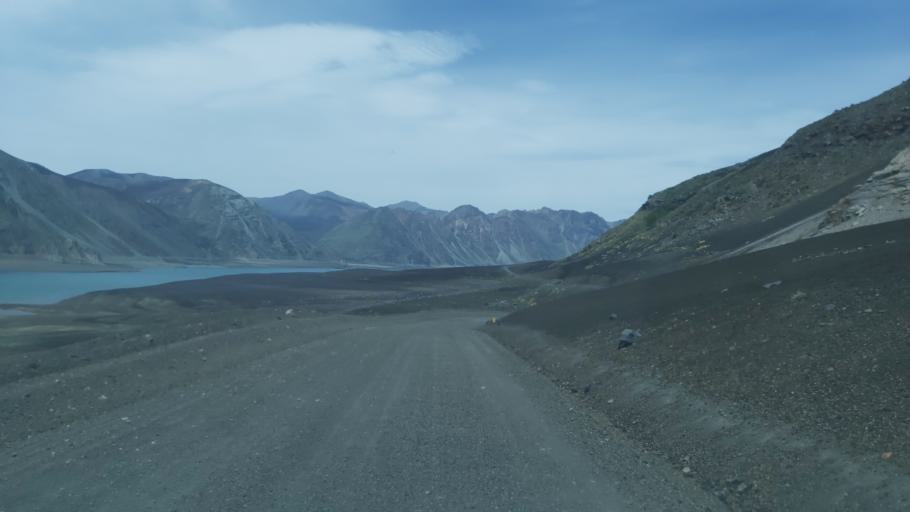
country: AR
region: Neuquen
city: Andacollo
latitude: -37.4043
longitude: -71.3015
